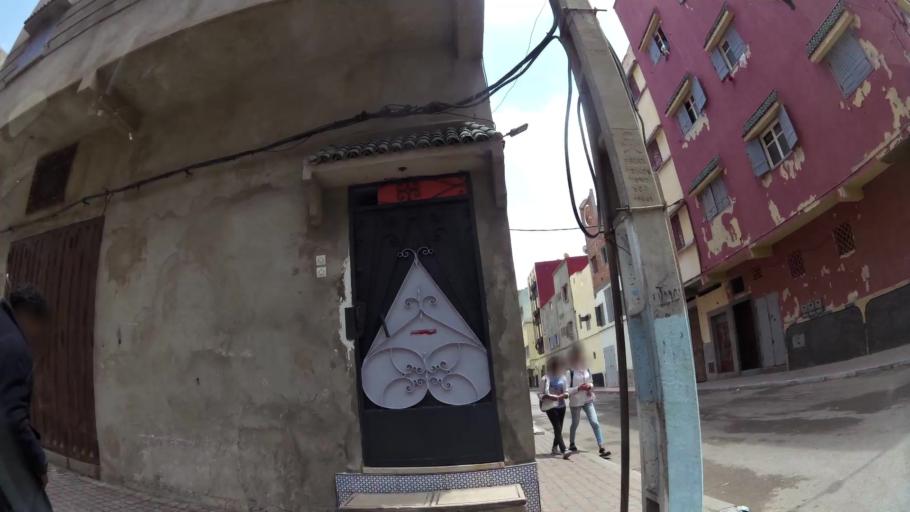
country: MA
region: Rabat-Sale-Zemmour-Zaer
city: Sale
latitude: 34.0525
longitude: -6.8226
